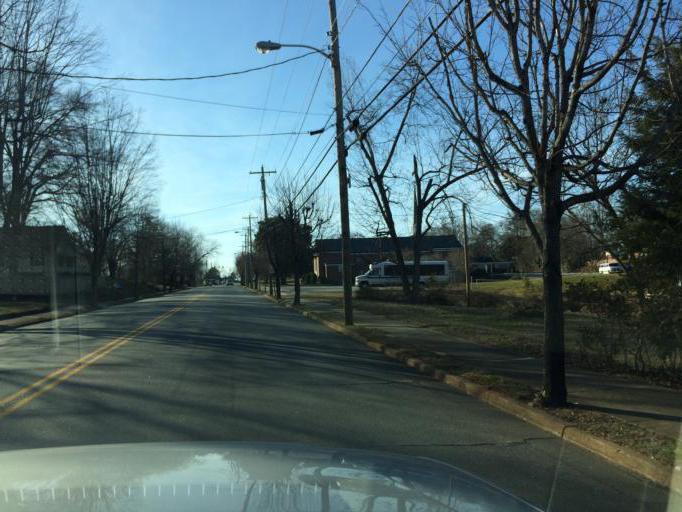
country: US
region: North Carolina
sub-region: Rutherford County
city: Forest City
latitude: 35.3322
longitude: -81.8551
